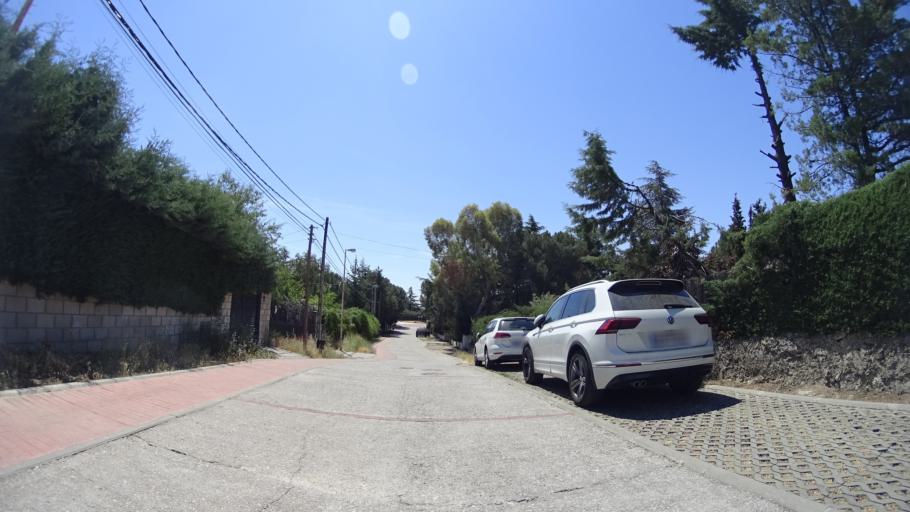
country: ES
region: Madrid
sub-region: Provincia de Madrid
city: Colmenarejo
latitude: 40.5578
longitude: -4.0096
